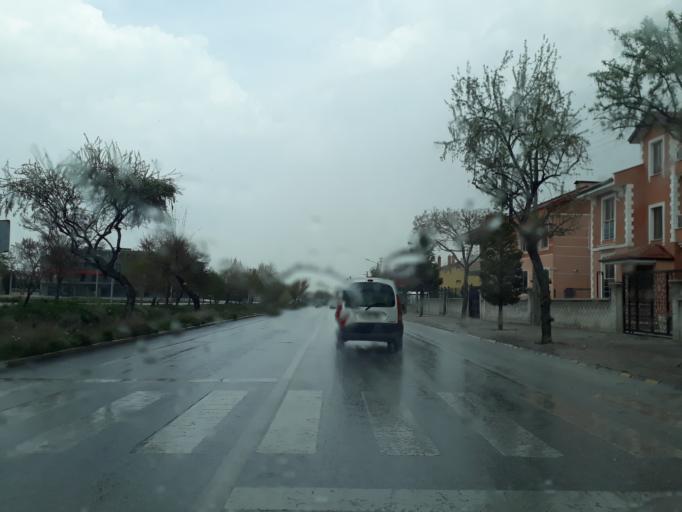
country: TR
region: Konya
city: Selcuklu
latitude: 37.9194
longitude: 32.4844
